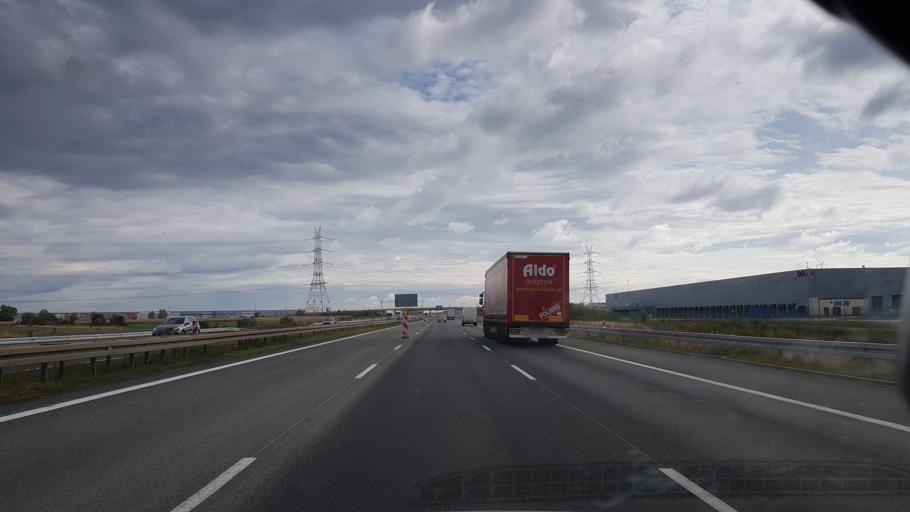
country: PL
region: Greater Poland Voivodeship
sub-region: Powiat poznanski
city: Komorniki
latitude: 52.3503
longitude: 16.7959
